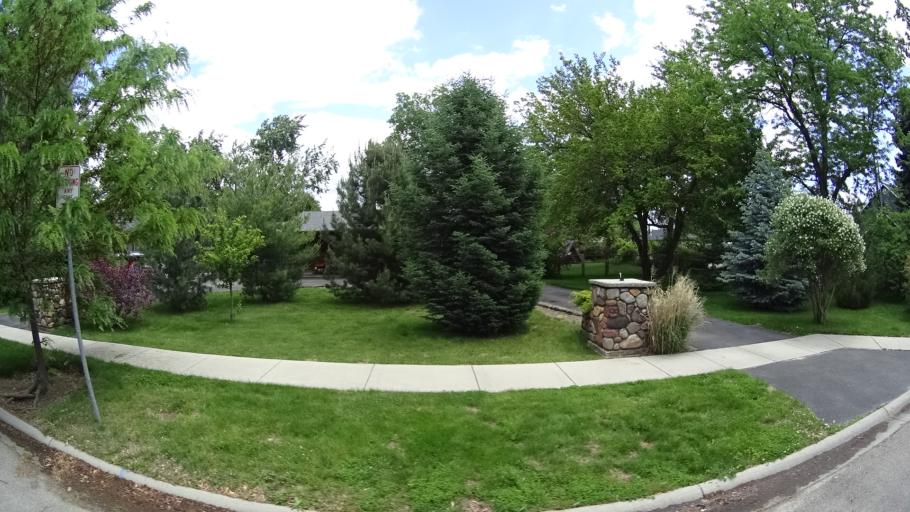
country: US
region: Idaho
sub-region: Ada County
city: Boise
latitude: 43.5879
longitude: -116.1986
